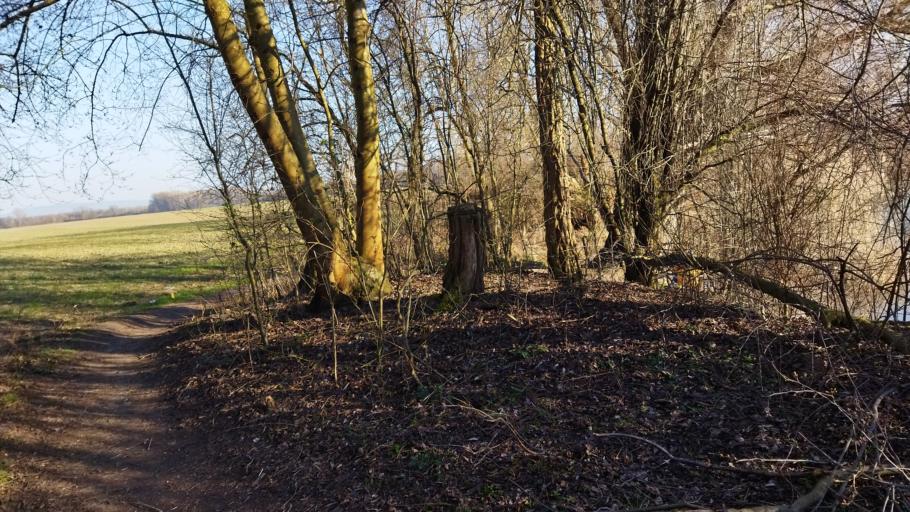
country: DE
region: Rheinland-Pfalz
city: Waldsee
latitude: 49.4137
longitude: 8.4503
